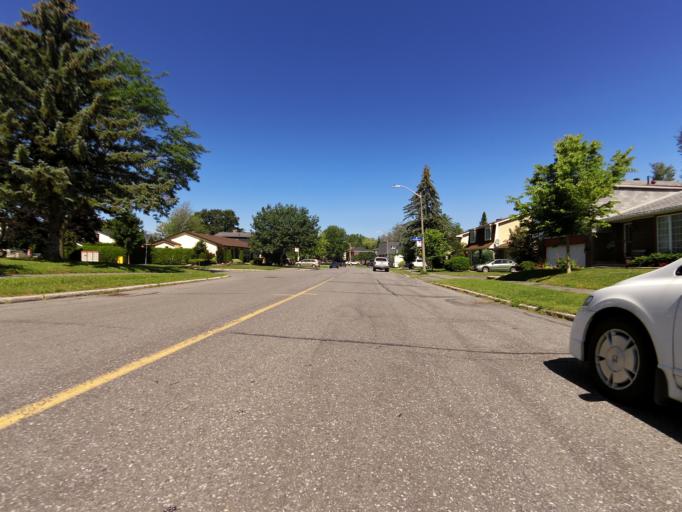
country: CA
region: Ontario
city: Ottawa
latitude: 45.3555
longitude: -75.6612
